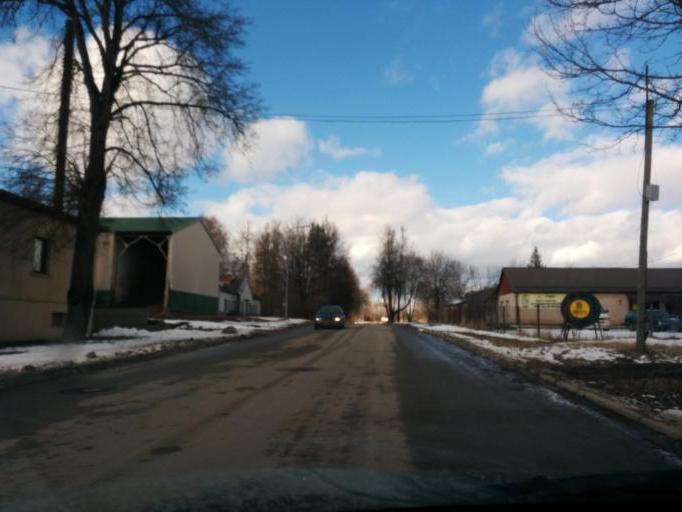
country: LV
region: Balvu Rajons
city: Balvi
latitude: 57.1395
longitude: 27.2578
